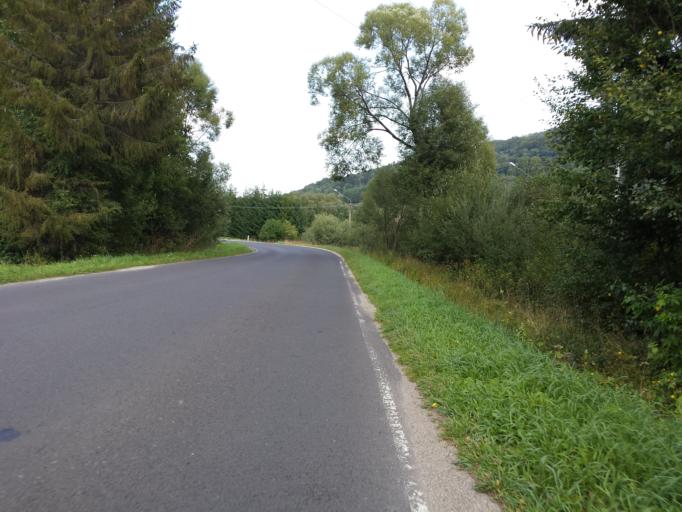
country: PL
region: Subcarpathian Voivodeship
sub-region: Powiat leski
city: Cisna
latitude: 49.1903
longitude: 22.4268
